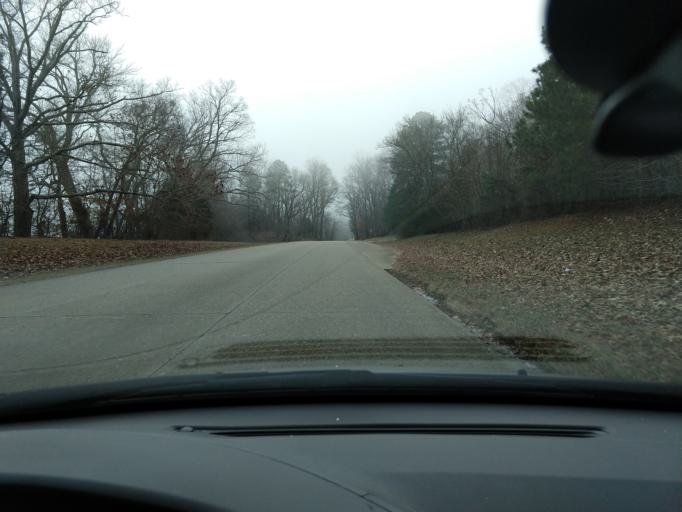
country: US
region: Virginia
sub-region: York County
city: Yorktown
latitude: 37.2456
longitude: -76.5287
